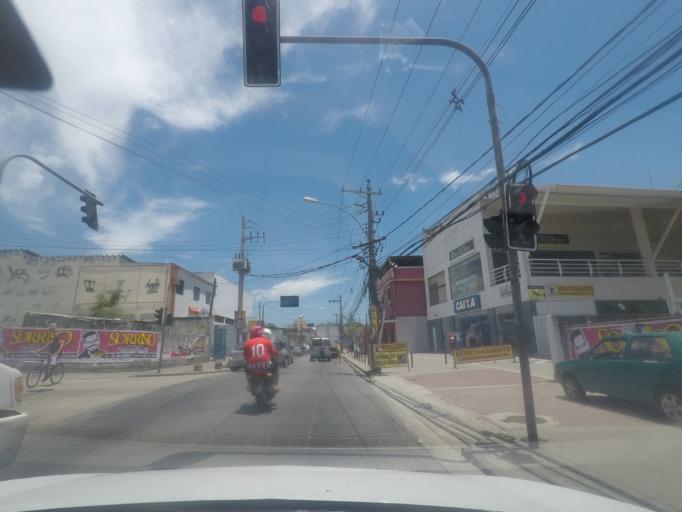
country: BR
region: Rio de Janeiro
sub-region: Itaguai
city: Itaguai
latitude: -22.9136
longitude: -43.6871
